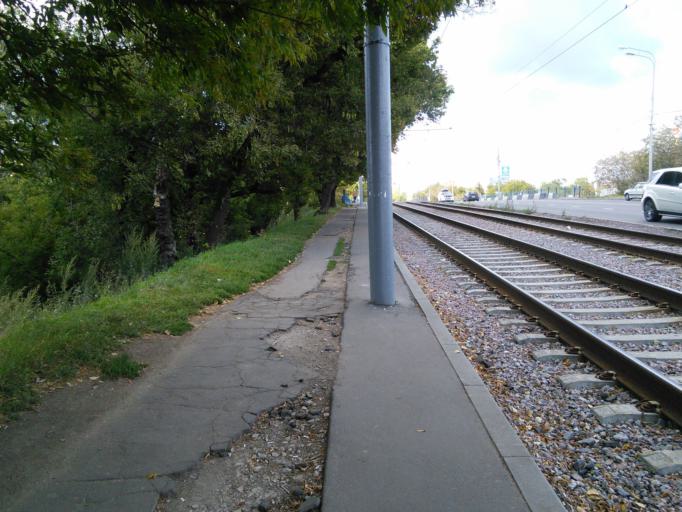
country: RU
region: Moskovskaya
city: Bogorodskoye
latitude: 55.8149
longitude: 37.7383
